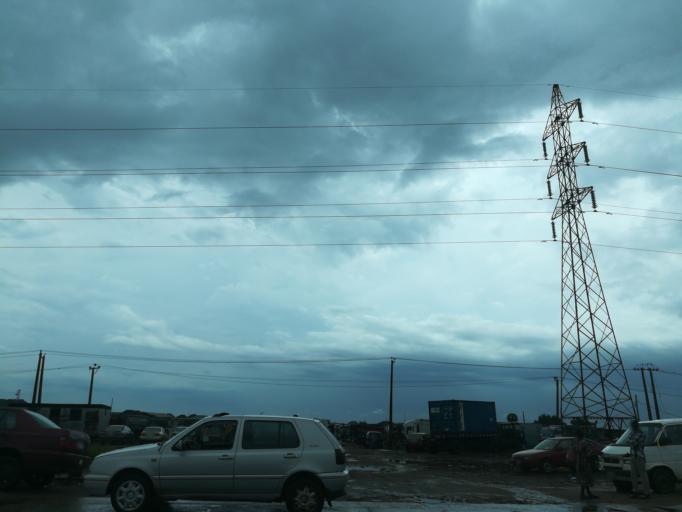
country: NG
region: Lagos
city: Ojota
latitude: 6.6058
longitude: 3.4070
